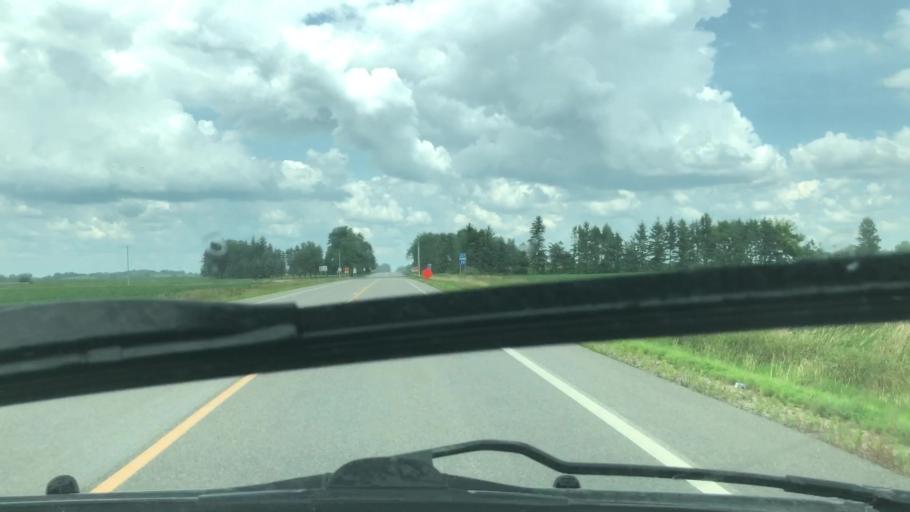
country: US
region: Minnesota
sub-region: Olmsted County
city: Stewartville
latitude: 43.8898
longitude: -92.5285
